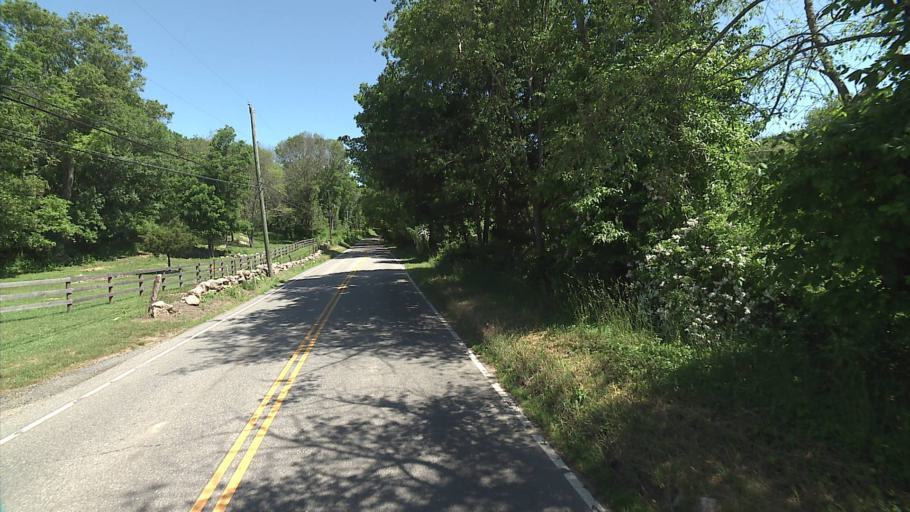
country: US
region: Rhode Island
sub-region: Washington County
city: Hopkinton
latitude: 41.4598
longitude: -71.8358
